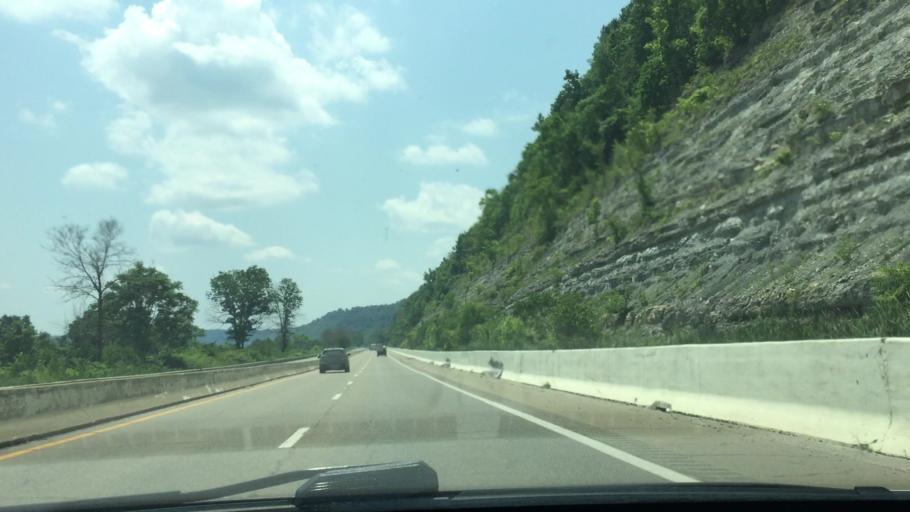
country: US
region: West Virginia
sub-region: Marshall County
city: Glendale
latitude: 39.9448
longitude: -80.7645
